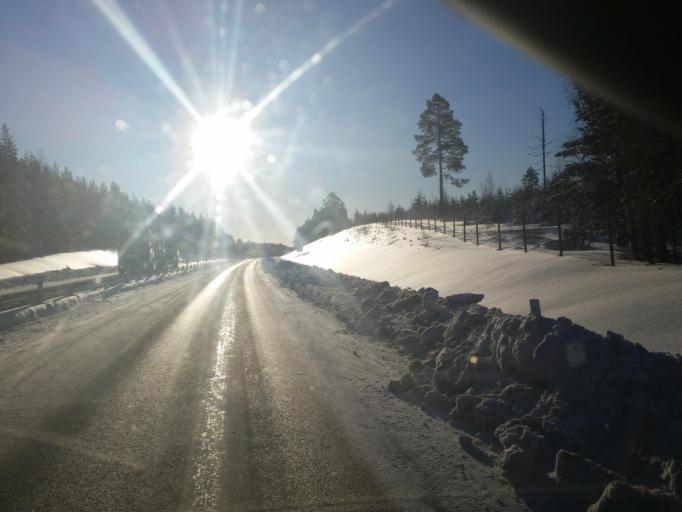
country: SE
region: Norrbotten
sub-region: Pitea Kommun
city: Pitea
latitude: 65.2432
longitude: 21.4905
